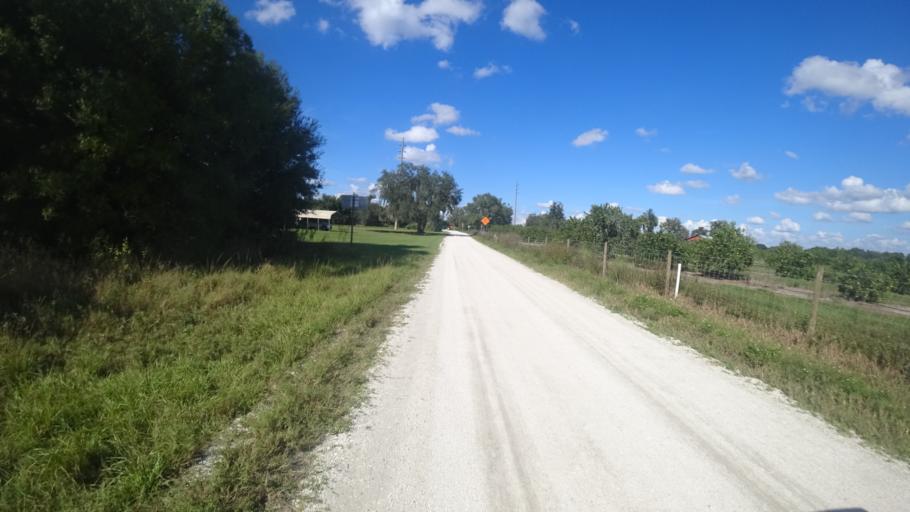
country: US
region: Florida
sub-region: Hardee County
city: Wauchula
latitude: 27.4718
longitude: -82.0554
